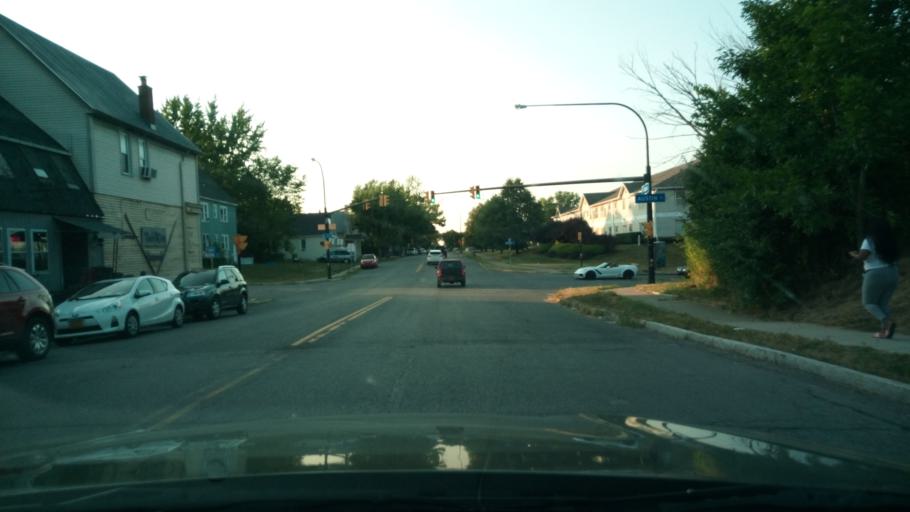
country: US
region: New York
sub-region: Erie County
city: Kenmore
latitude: 42.9393
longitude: -78.8984
